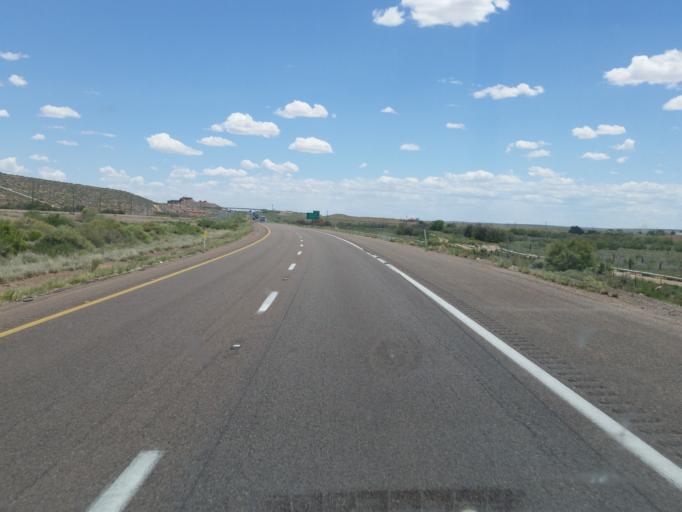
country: US
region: Arizona
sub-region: Navajo County
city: Joseph City
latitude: 34.9315
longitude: -110.2731
